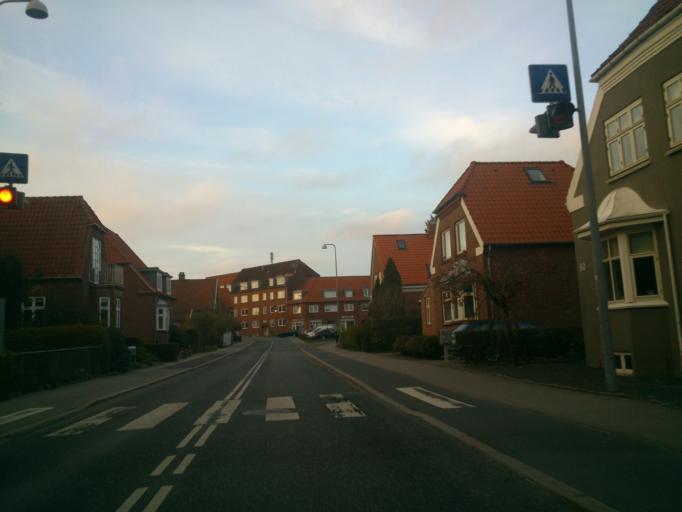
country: DK
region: South Denmark
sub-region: Fredericia Kommune
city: Fredericia
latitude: 55.5716
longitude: 9.7599
